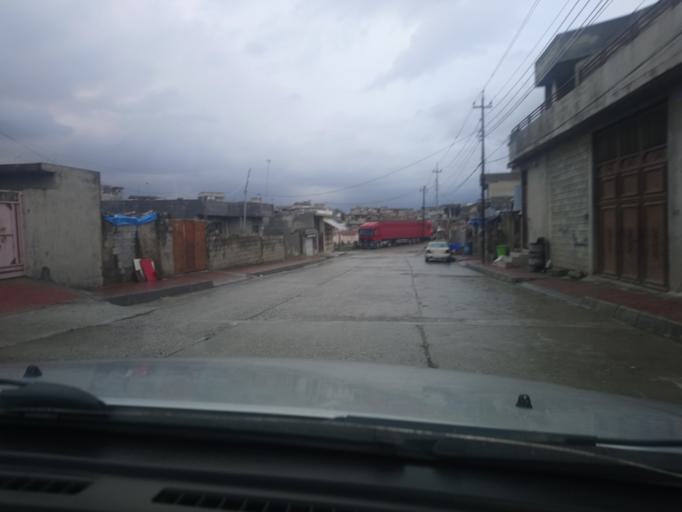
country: IQ
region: As Sulaymaniyah
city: Qeladize
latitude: 36.1910
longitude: 45.1238
